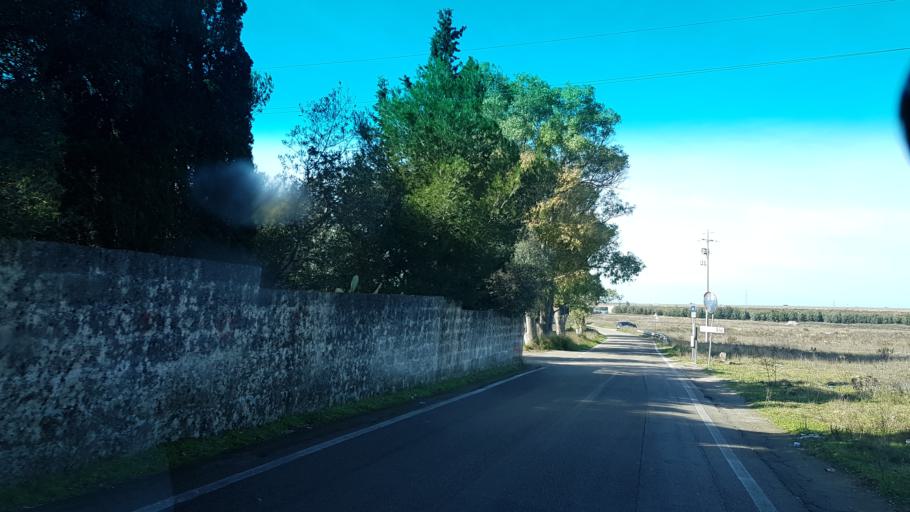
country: IT
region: Apulia
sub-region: Provincia di Lecce
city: Lecce
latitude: 40.3493
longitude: 18.1324
